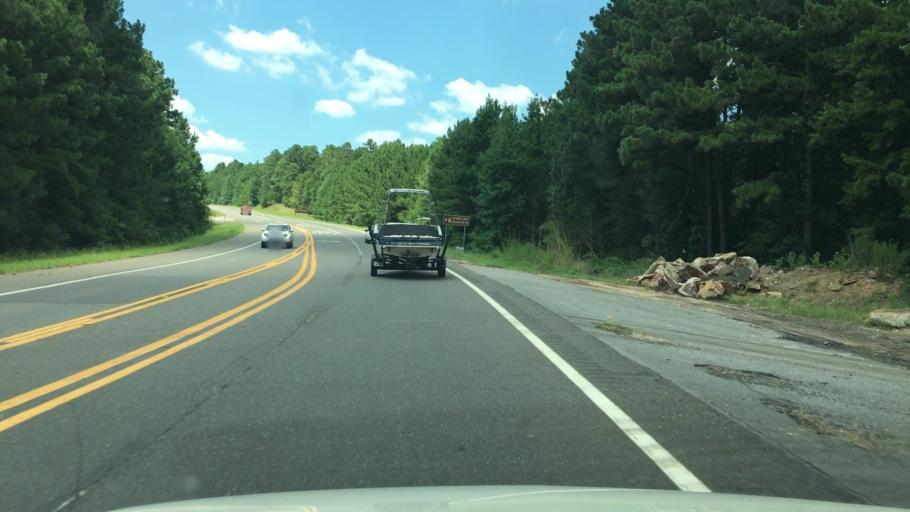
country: US
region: Arkansas
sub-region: Clark County
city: Arkadelphia
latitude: 34.2091
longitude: -93.0797
